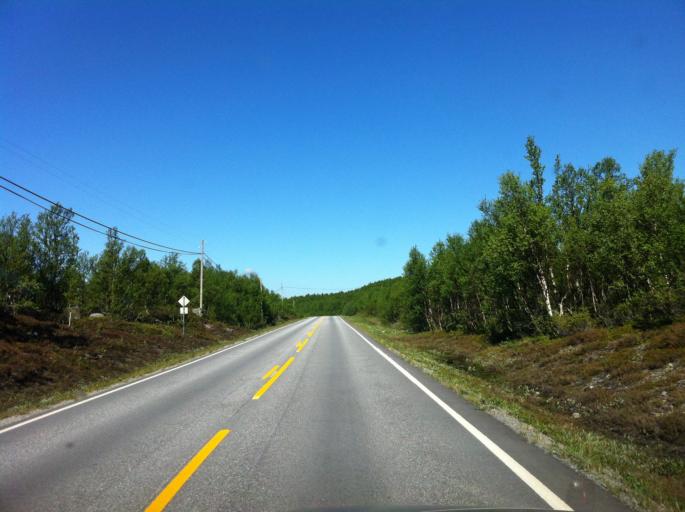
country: NO
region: Sor-Trondelag
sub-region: Tydal
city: Aas
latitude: 62.6355
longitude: 11.9567
